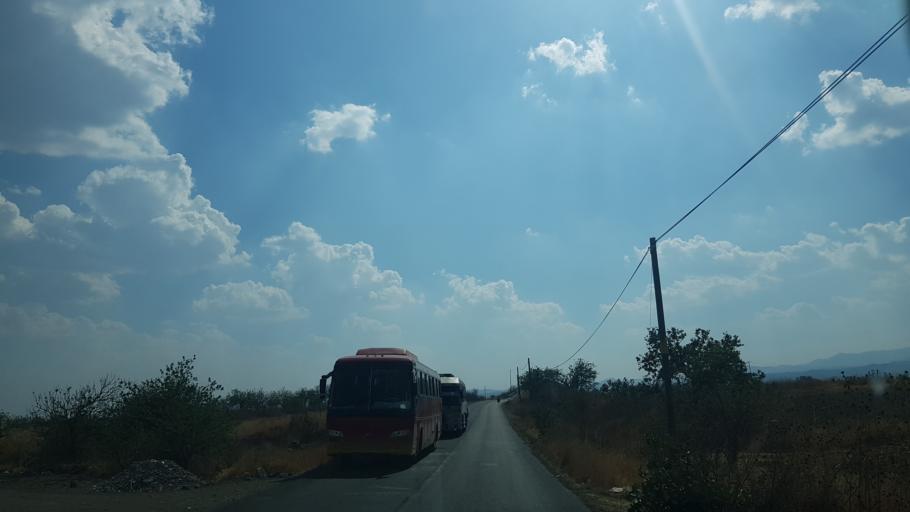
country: MX
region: Puebla
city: Atlixco
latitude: 18.9024
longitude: -98.4871
